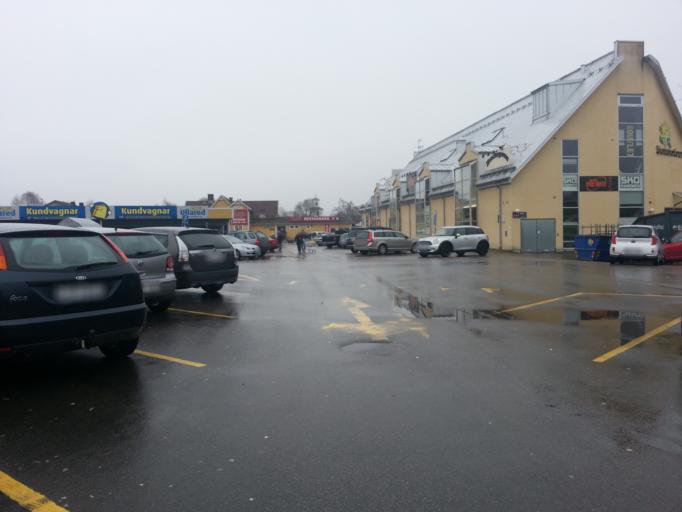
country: SE
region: Halland
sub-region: Falkenbergs Kommun
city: Falkenberg
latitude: 57.1357
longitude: 12.7123
